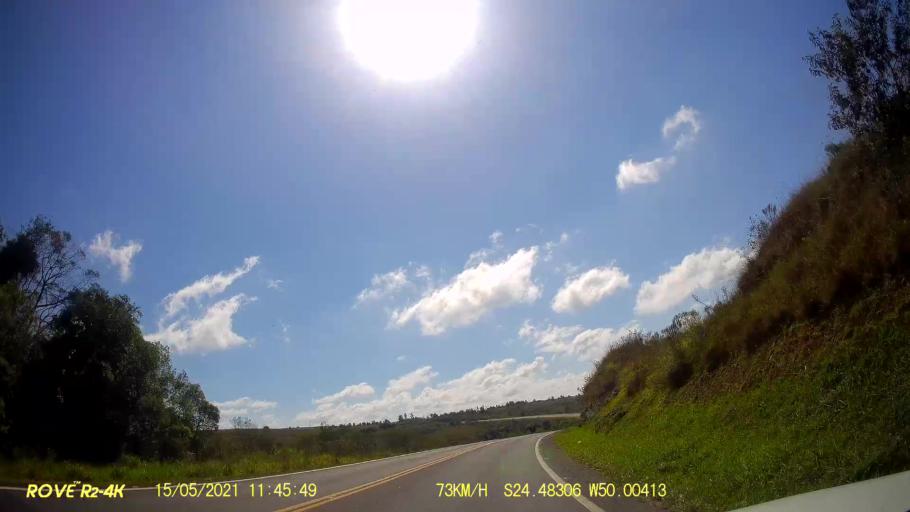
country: BR
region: Parana
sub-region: Pirai Do Sul
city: Pirai do Sul
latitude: -24.4832
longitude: -50.0043
